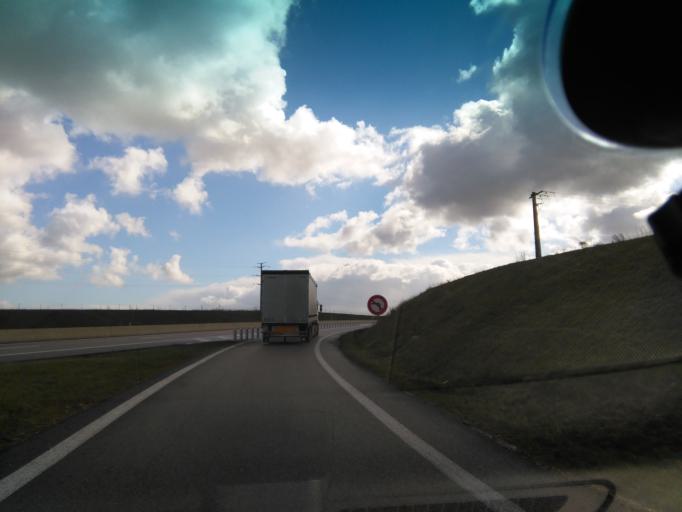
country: FR
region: Lower Normandy
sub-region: Departement de l'Orne
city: Argentan
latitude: 48.7204
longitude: -0.0581
